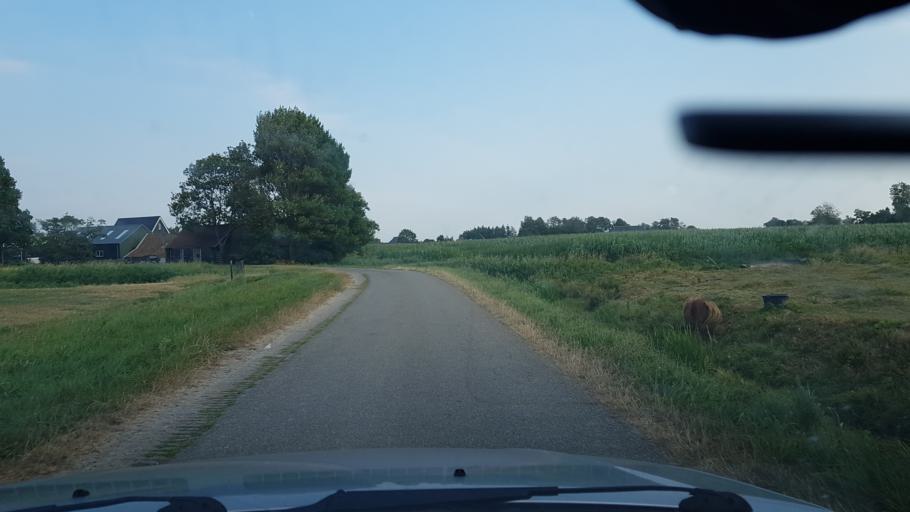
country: NL
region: Friesland
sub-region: Gemeente Dongeradeel
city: Holwerd
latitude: 53.3507
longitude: 5.8744
